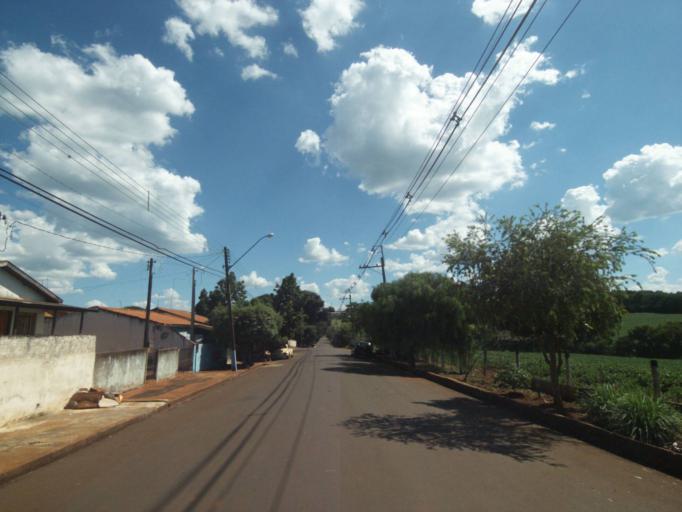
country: BR
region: Parana
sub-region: Sertanopolis
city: Sertanopolis
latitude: -23.0370
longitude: -50.8213
